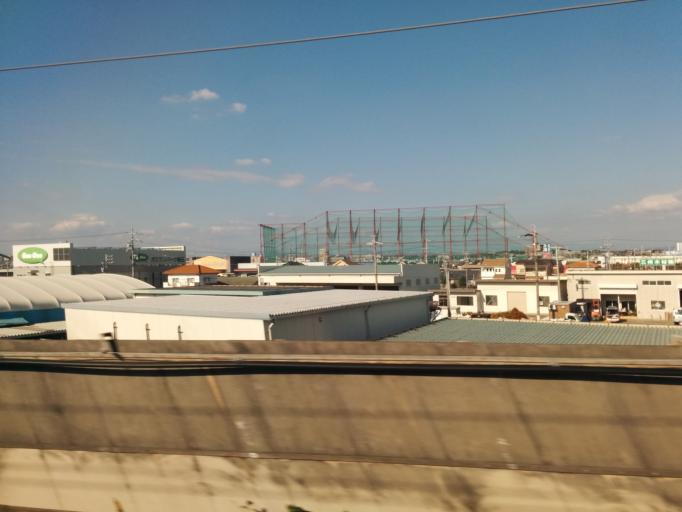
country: JP
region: Shizuoka
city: Iwata
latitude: 34.7080
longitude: 137.8661
